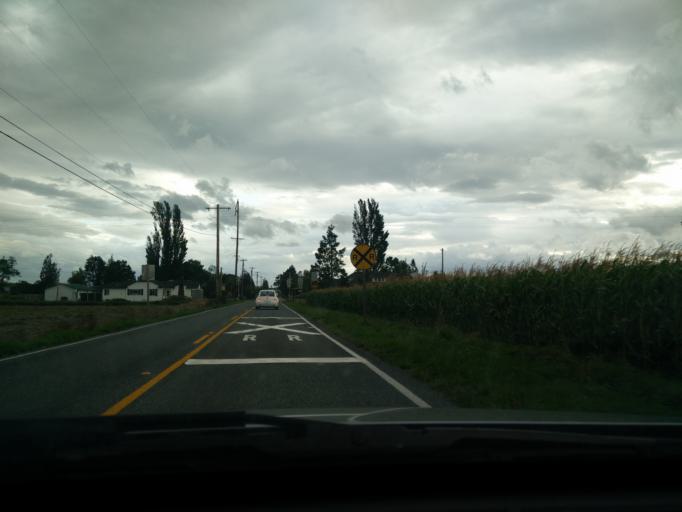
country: US
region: Washington
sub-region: Snohomish County
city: Stanwood
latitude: 48.2480
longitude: -122.3708
